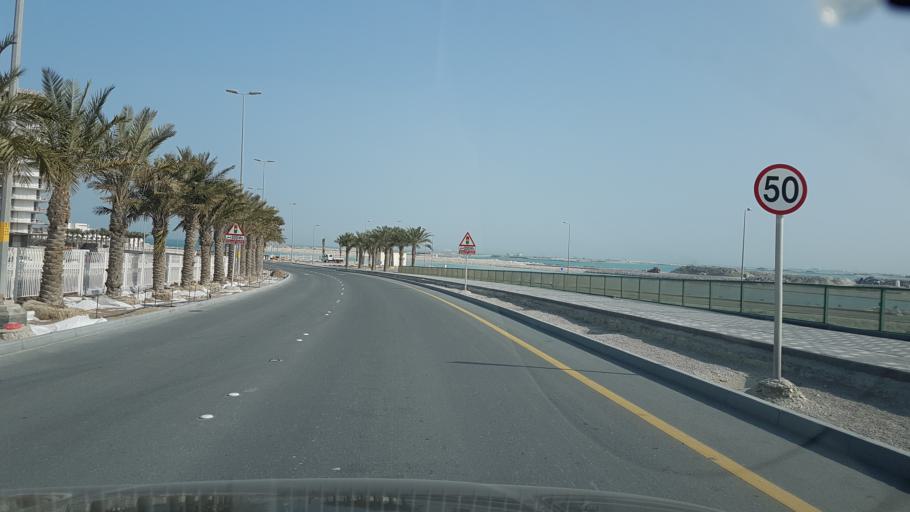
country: BH
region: Muharraq
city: Al Hadd
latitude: 26.2688
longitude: 50.6717
